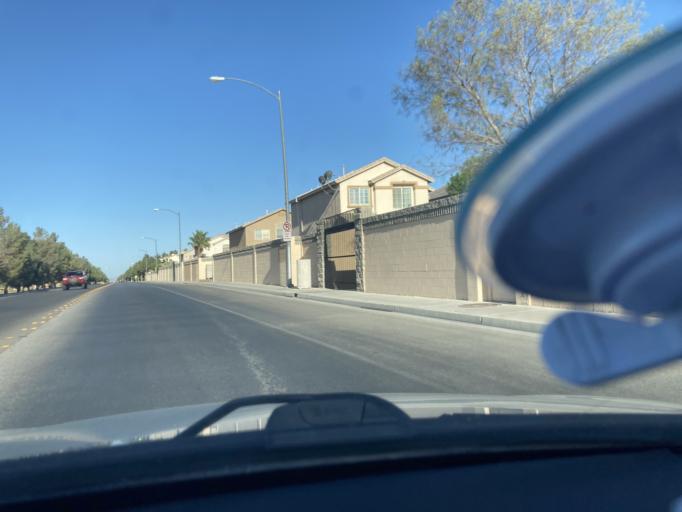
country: US
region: Nevada
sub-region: Clark County
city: Enterprise
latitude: 36.0592
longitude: -115.2927
